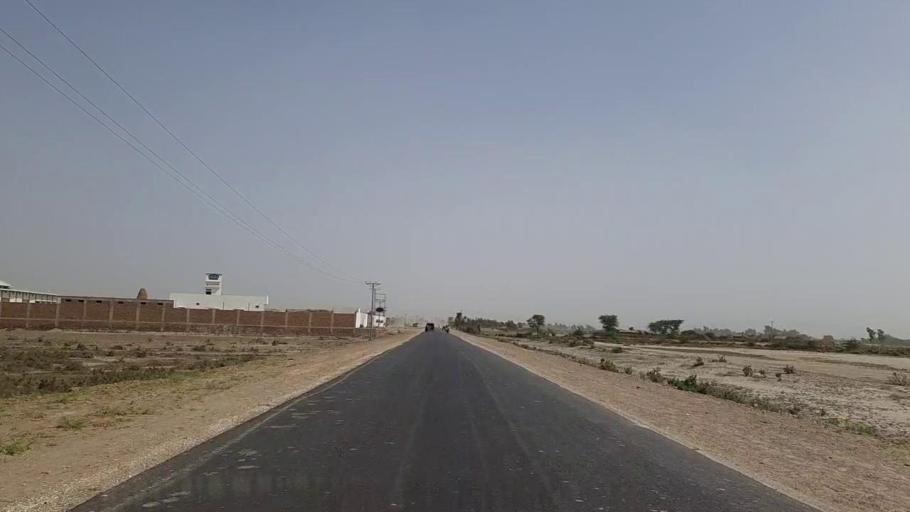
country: PK
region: Sindh
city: Tando Bago
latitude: 24.7990
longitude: 68.9449
